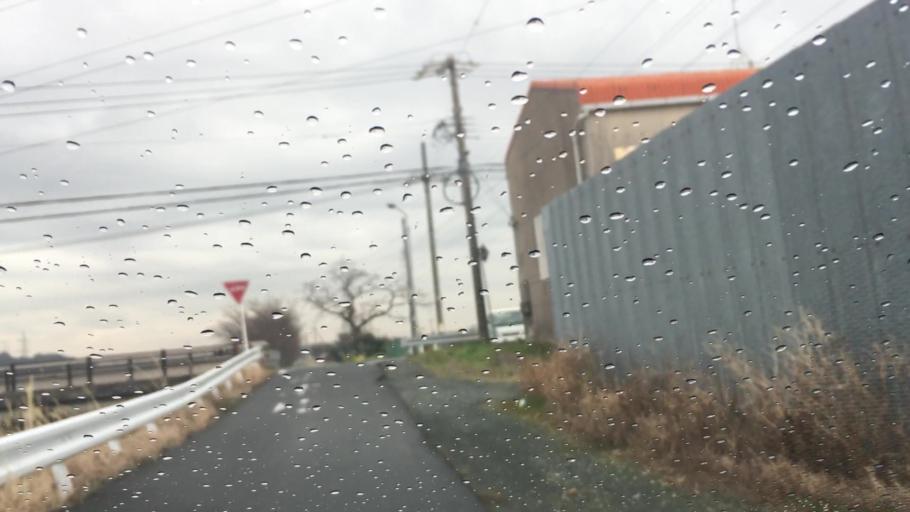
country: JP
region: Aichi
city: Toyohashi
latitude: 34.7064
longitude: 137.3916
